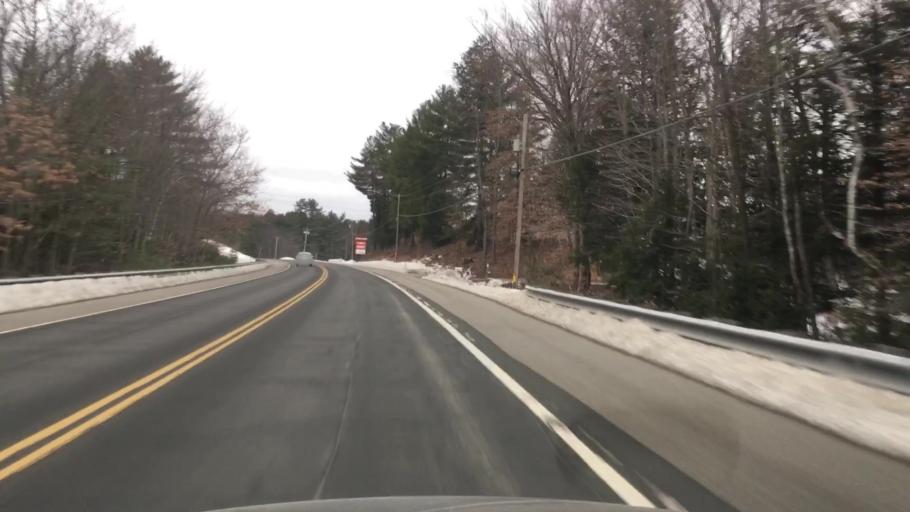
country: US
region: New Hampshire
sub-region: Merrimack County
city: Sutton
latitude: 43.2553
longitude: -71.9312
